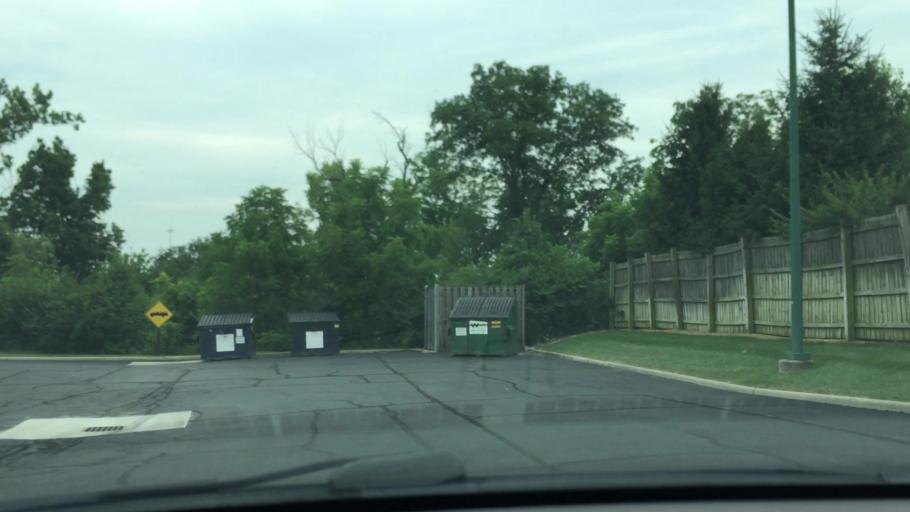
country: US
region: Ohio
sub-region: Franklin County
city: Reynoldsburg
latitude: 39.9360
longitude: -82.7930
